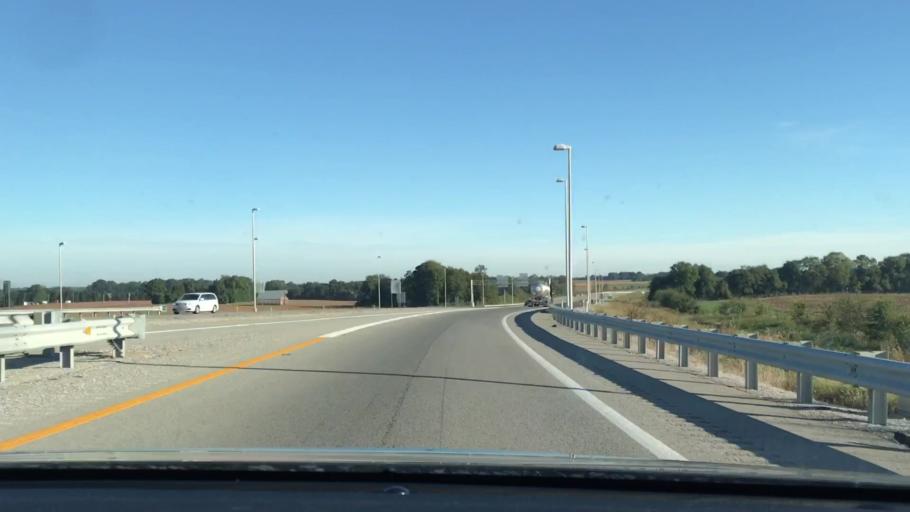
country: US
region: Kentucky
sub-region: Christian County
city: Fort Campbell North
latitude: 36.7462
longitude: -87.5102
